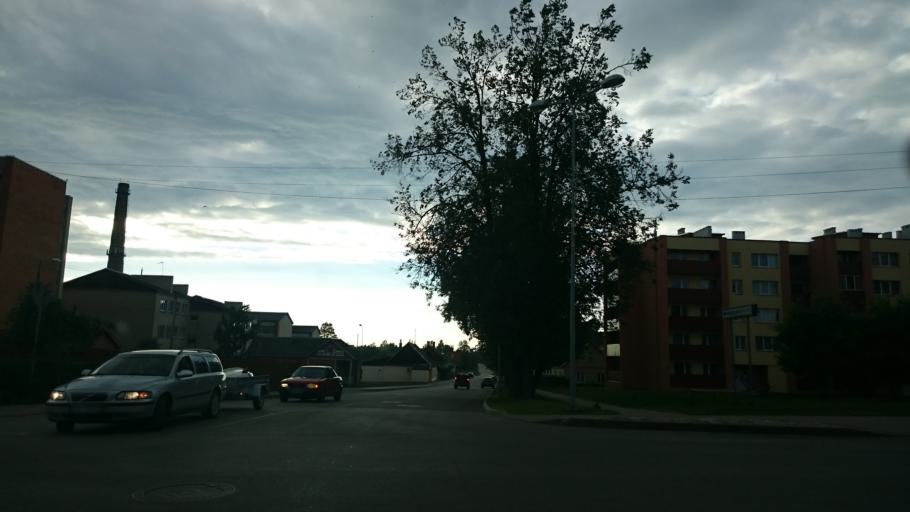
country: LV
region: Ludzas Rajons
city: Ludza
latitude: 56.5412
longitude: 27.7061
